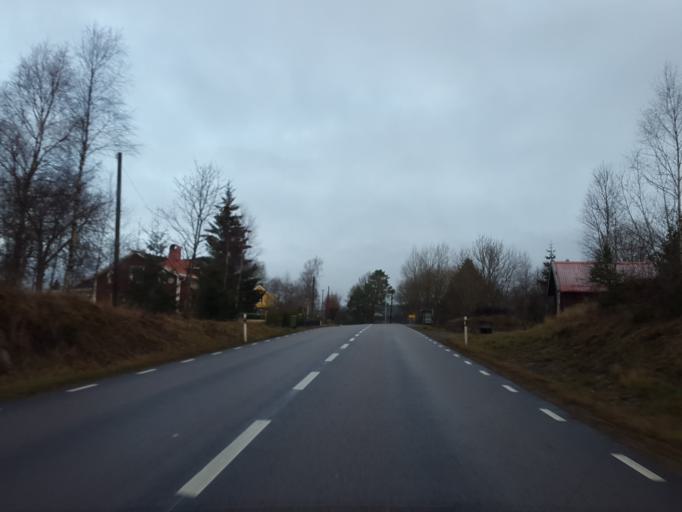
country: SE
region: Vaestra Goetaland
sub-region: Boras Kommun
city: Sandared
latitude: 57.8042
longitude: 12.7545
